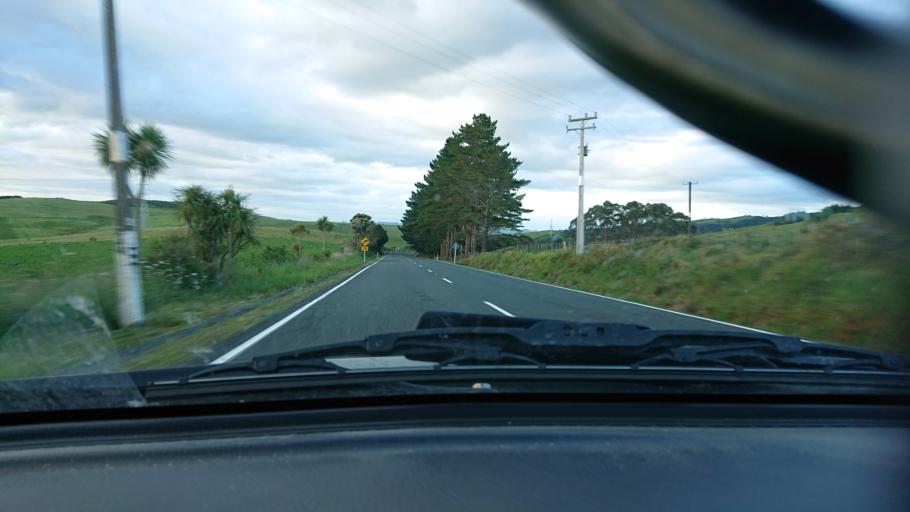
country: NZ
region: Auckland
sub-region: Auckland
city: Parakai
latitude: -36.4706
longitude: 174.4490
